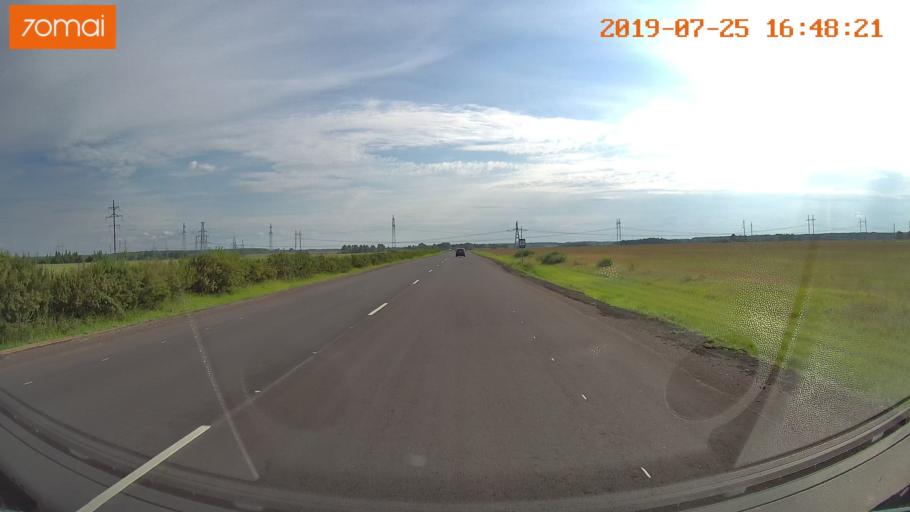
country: RU
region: Ivanovo
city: Privolzhsk
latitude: 57.3569
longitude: 41.2606
